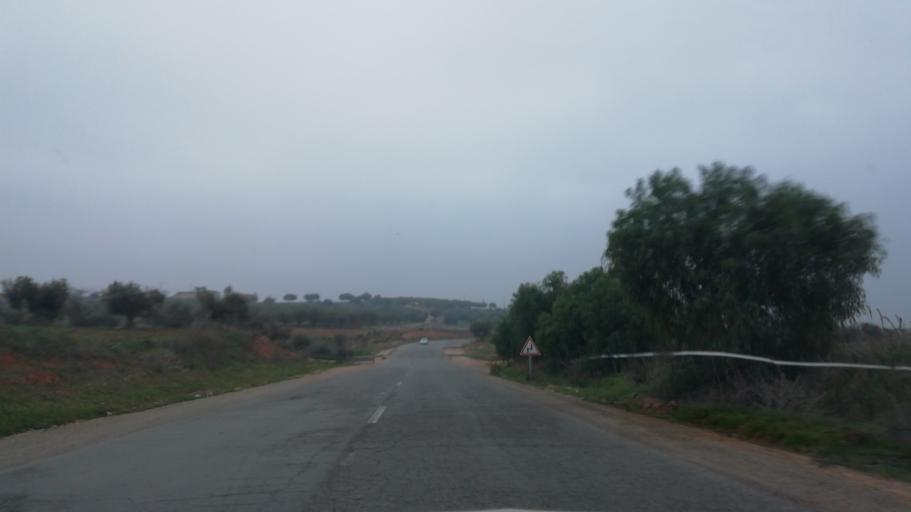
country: DZ
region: Mascara
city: Mascara
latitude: 35.3889
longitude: 0.1616
